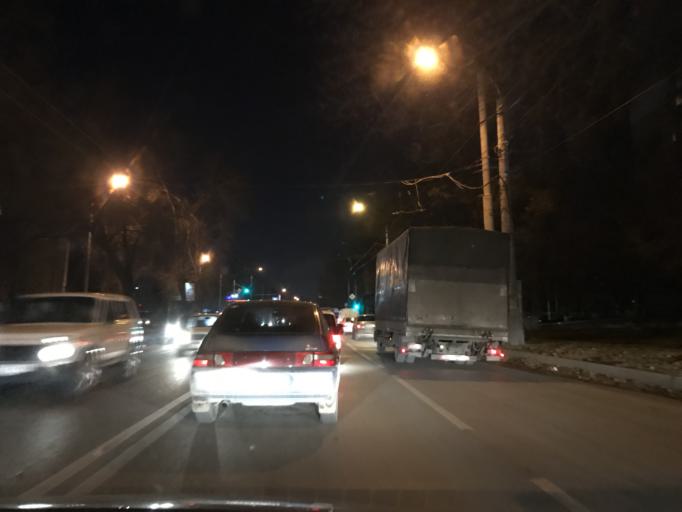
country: RU
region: Rostov
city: Kalinin
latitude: 47.2024
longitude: 39.6135
